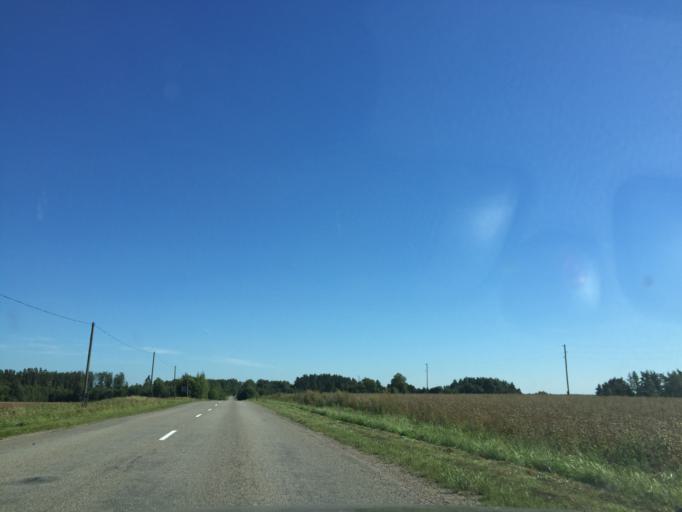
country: LV
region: Akniste
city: Akniste
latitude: 56.1441
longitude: 25.7998
